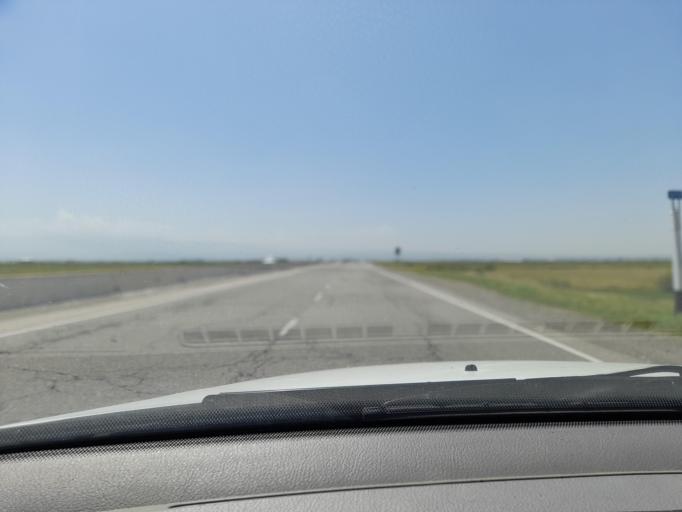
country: UZ
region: Jizzax
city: Paxtakor
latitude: 40.2033
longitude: 67.9789
